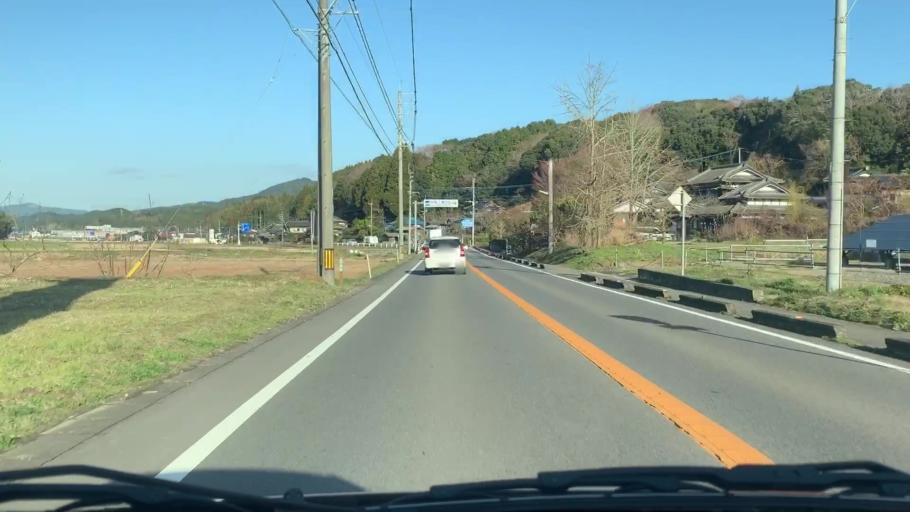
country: JP
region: Saga Prefecture
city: Takeocho-takeo
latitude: 33.2461
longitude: 130.0050
